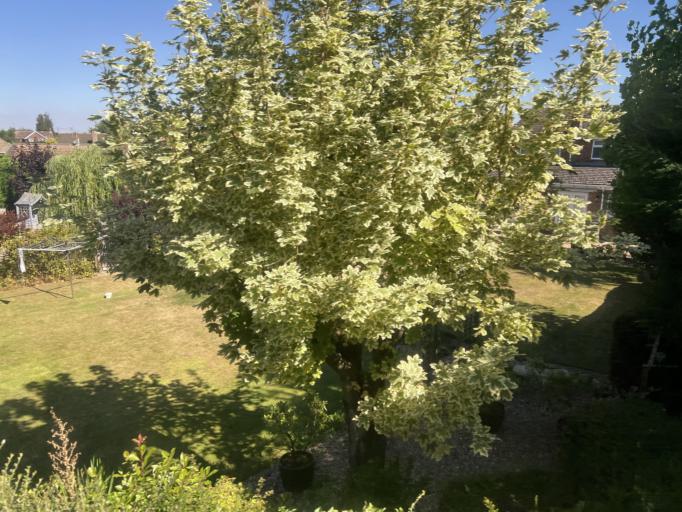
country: GB
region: England
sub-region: Lincolnshire
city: Boston
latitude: 52.9716
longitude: -0.0545
